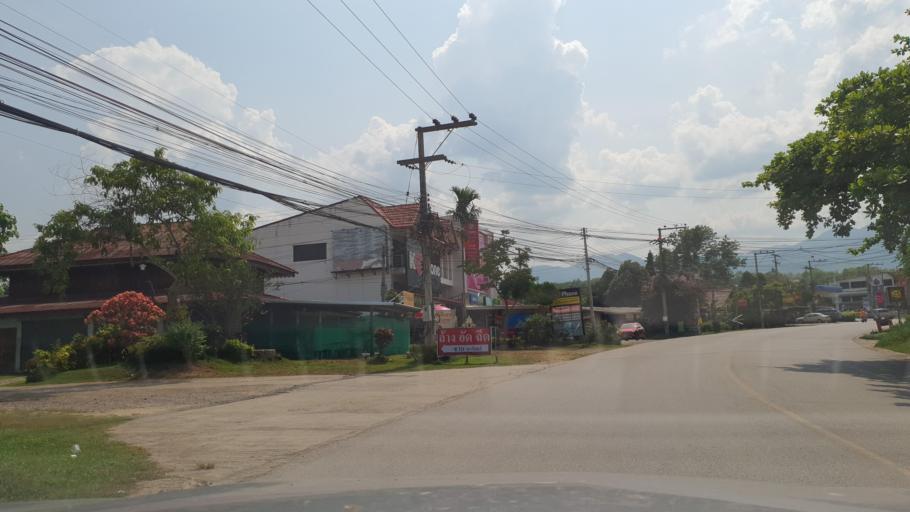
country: TH
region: Chiang Mai
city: Pai
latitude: 19.3552
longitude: 98.4388
